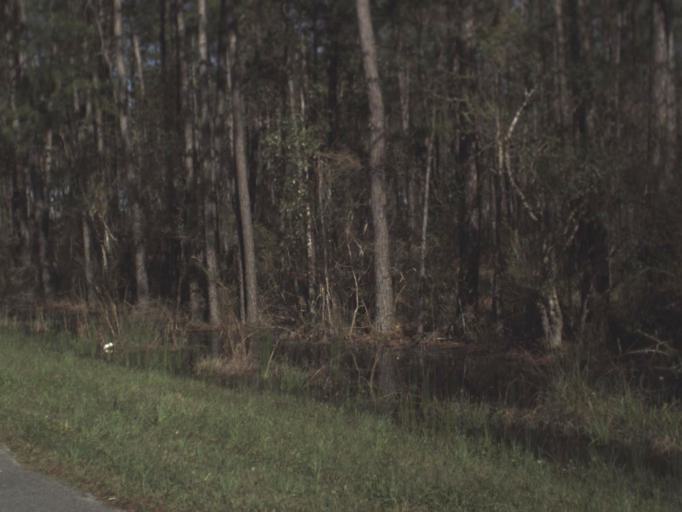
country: US
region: Florida
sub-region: Gulf County
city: Wewahitchka
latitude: 29.9517
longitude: -85.1810
